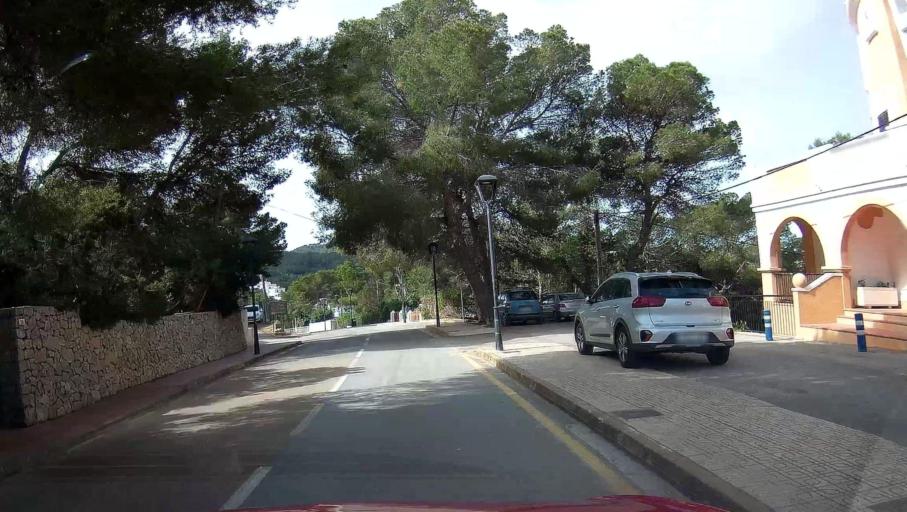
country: ES
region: Balearic Islands
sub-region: Illes Balears
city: Sant Joan de Labritja
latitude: 39.1121
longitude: 1.5174
